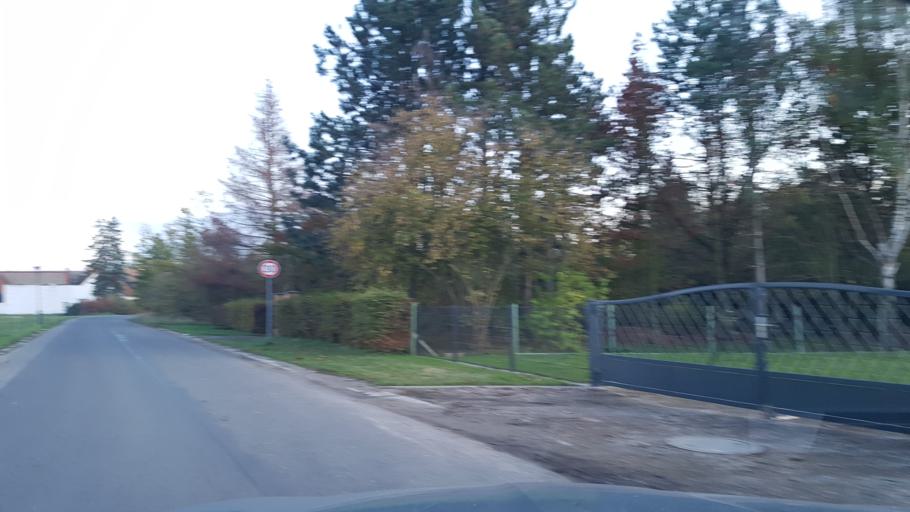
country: DE
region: Brandenburg
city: Doberlug-Kirchhain
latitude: 51.6439
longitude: 13.5641
